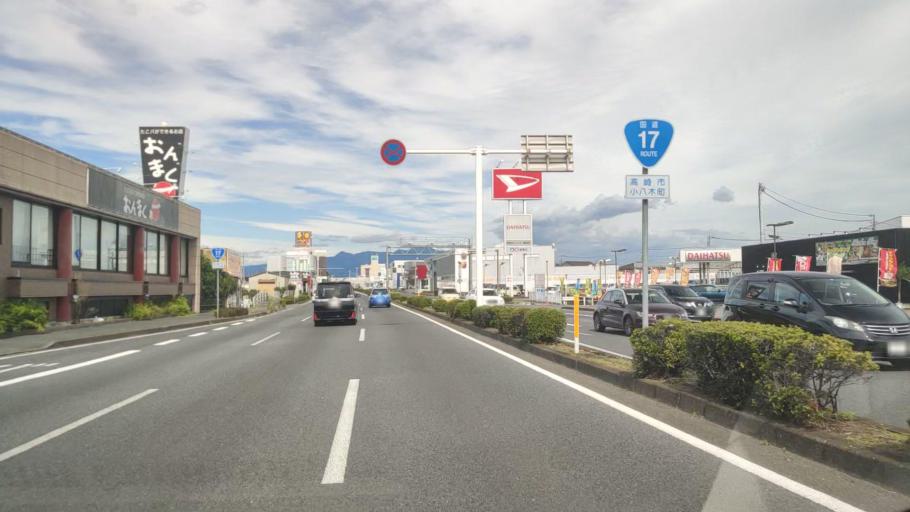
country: JP
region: Gunma
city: Takasaki
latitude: 36.3583
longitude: 139.0154
